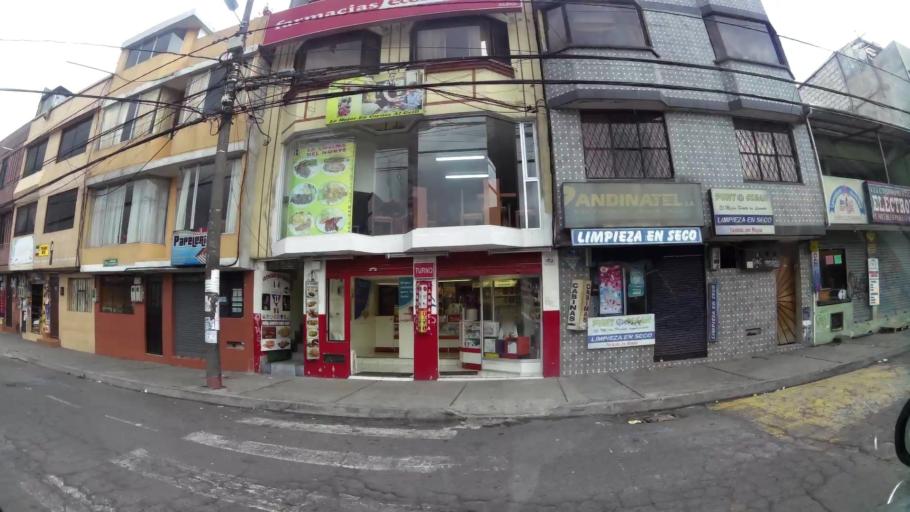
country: EC
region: Pichincha
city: Quito
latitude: -0.2678
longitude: -78.5374
